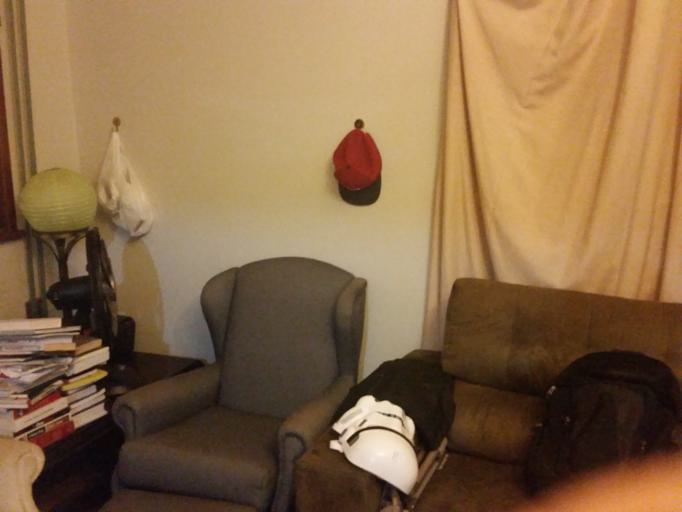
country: BR
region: Rio Grande do Sul
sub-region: Porto Alegre
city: Porto Alegre
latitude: -30.0178
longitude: -51.1899
